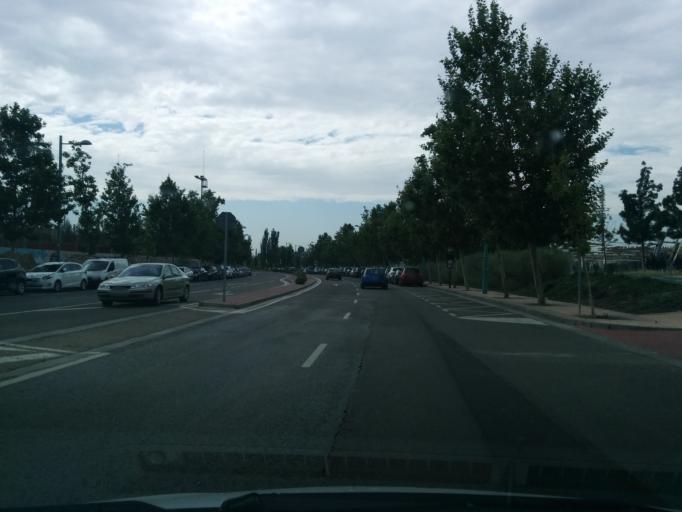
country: ES
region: Aragon
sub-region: Provincia de Zaragoza
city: Almozara
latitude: 41.6682
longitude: -0.8962
